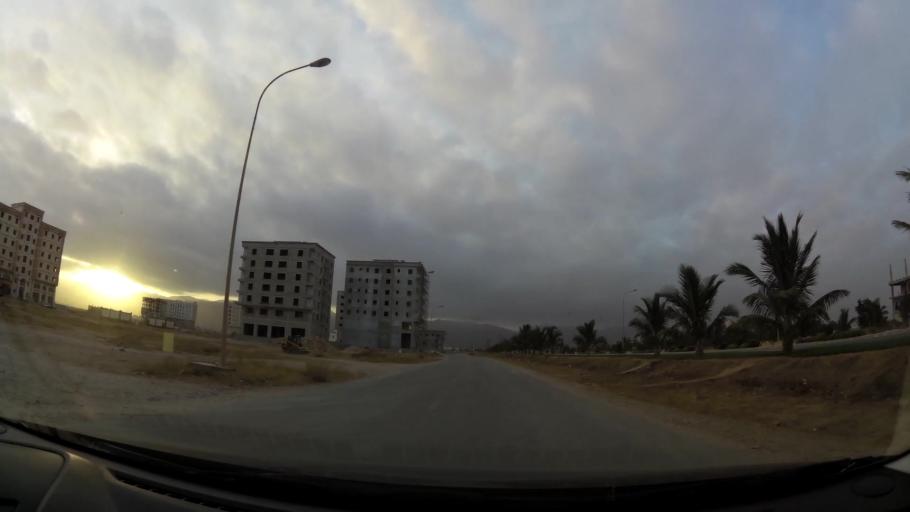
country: OM
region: Zufar
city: Salalah
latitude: 17.0250
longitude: 54.0321
